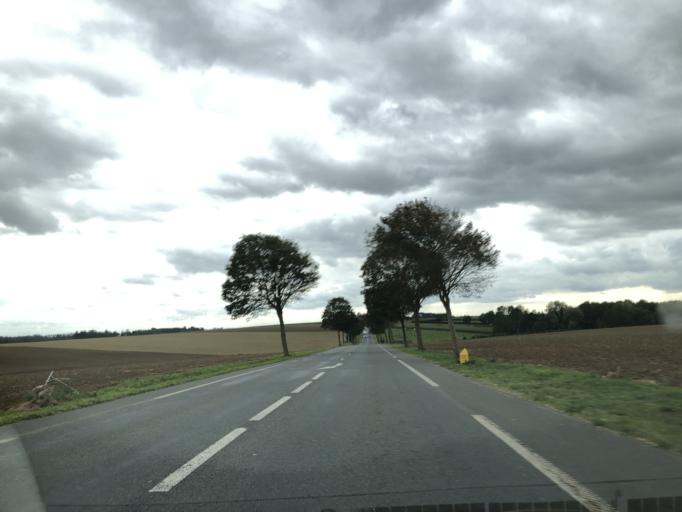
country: FR
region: Nord-Pas-de-Calais
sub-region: Departement du Pas-de-Calais
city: Fruges
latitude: 50.4709
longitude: 2.1088
